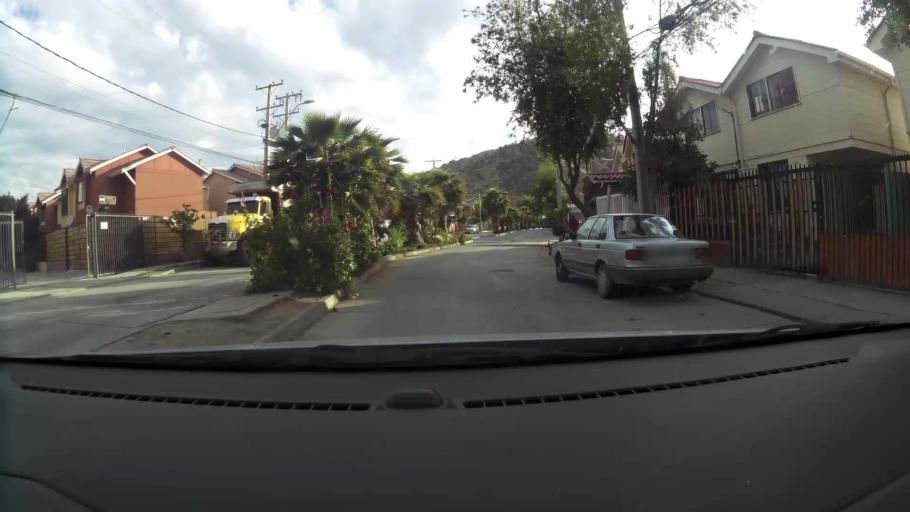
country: CL
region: Santiago Metropolitan
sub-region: Provincia de Maipo
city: San Bernardo
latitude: -33.6464
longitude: -70.6639
